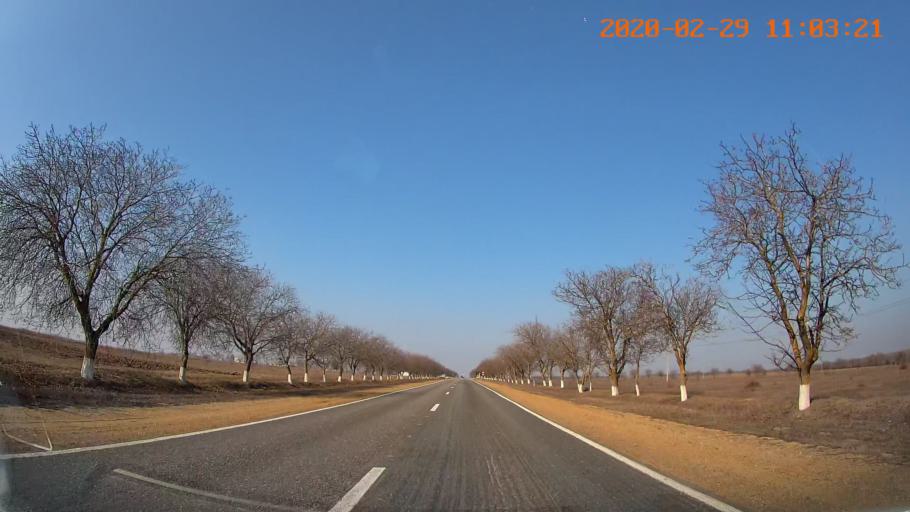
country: MD
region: Criuleni
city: Criuleni
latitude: 47.1790
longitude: 29.2191
